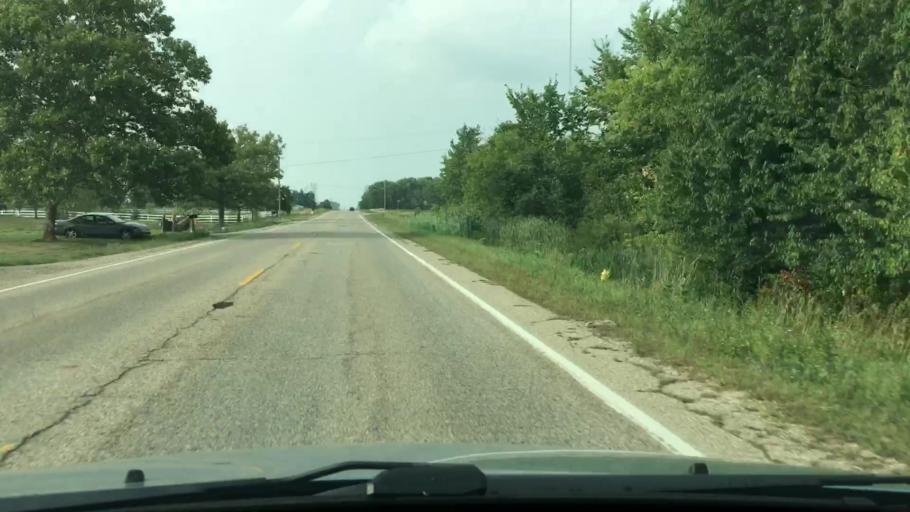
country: US
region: Michigan
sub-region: Ottawa County
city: Allendale
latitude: 42.9485
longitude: -85.9036
